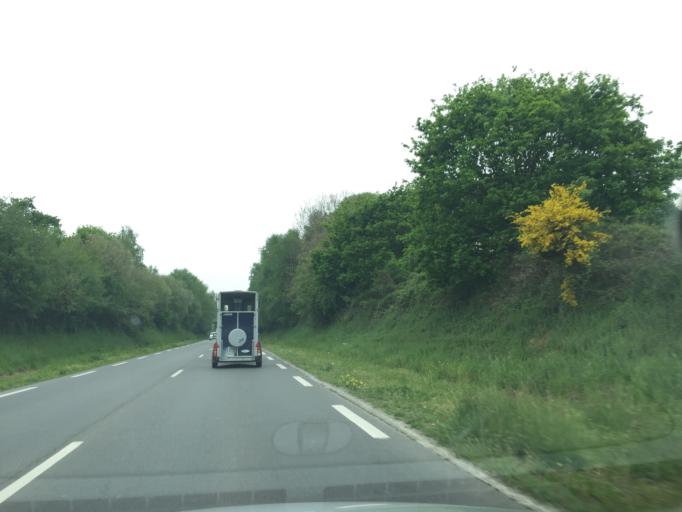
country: FR
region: Brittany
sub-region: Departement des Cotes-d'Armor
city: Lamballe
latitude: 48.4788
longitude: -2.5185
